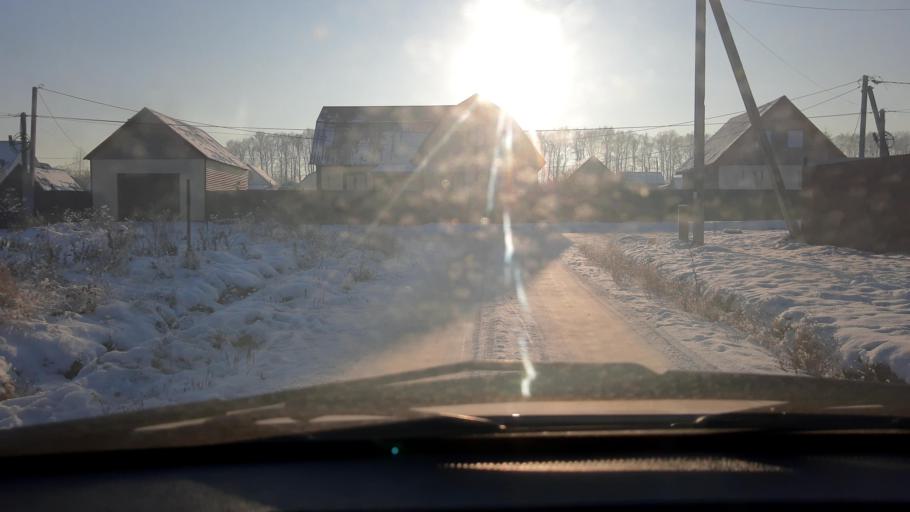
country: RU
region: Bashkortostan
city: Iglino
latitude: 54.8024
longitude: 56.3893
